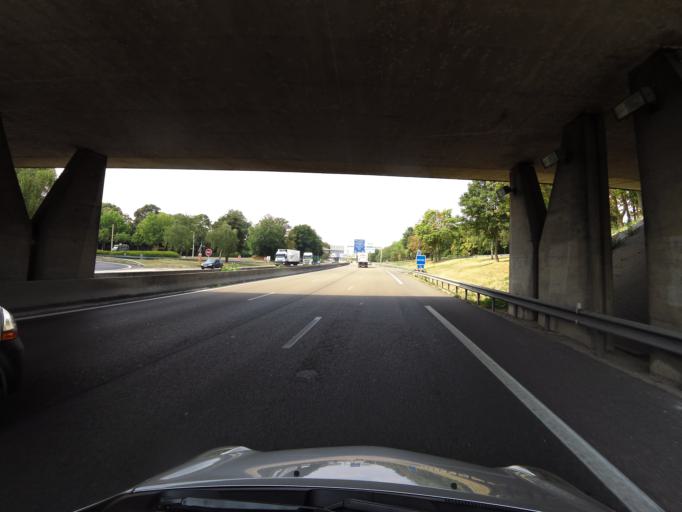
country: FR
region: Champagne-Ardenne
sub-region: Departement de la Marne
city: Reims
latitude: 49.2449
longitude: 4.0294
